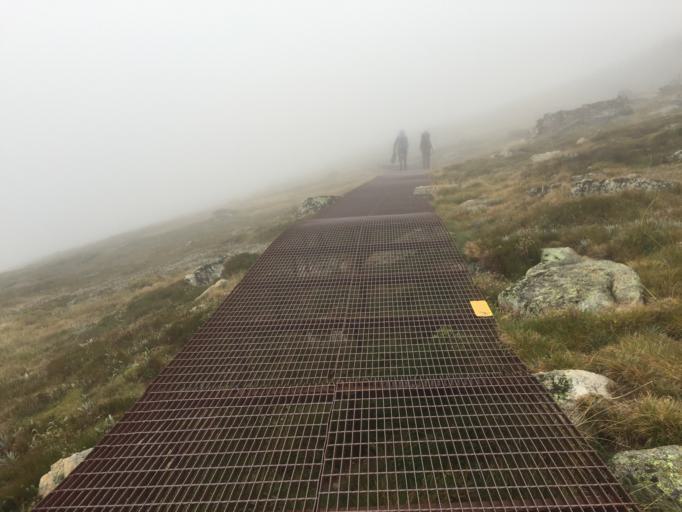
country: AU
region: New South Wales
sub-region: Snowy River
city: Jindabyne
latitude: -36.4628
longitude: 148.2699
